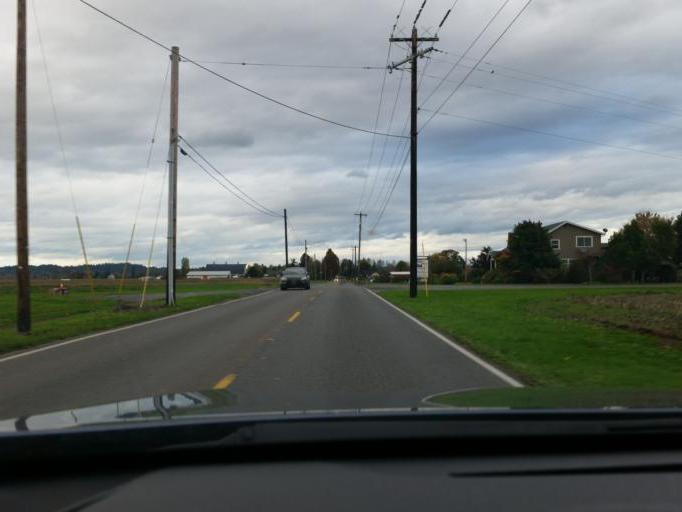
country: US
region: Washington
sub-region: Snohomish County
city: Cathcart
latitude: 47.8799
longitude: -122.0990
